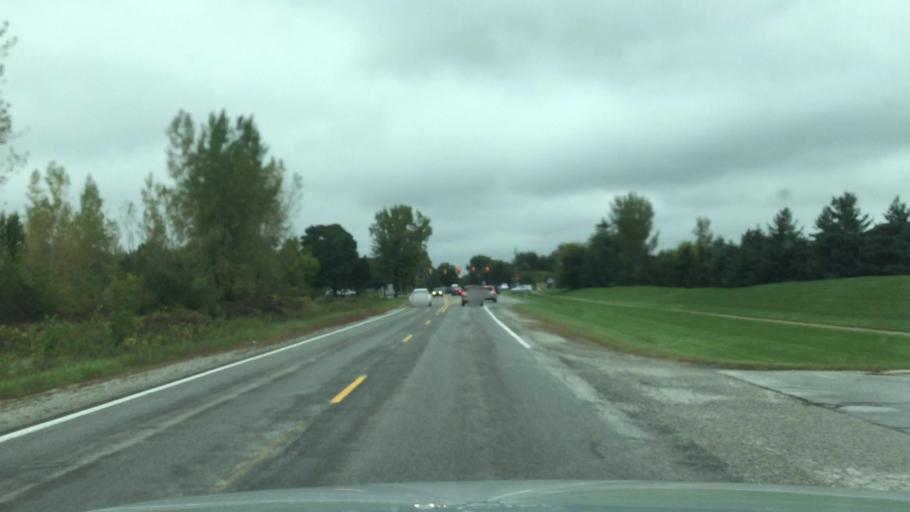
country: US
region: Michigan
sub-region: Saginaw County
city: Saginaw
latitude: 43.4674
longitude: -83.9952
